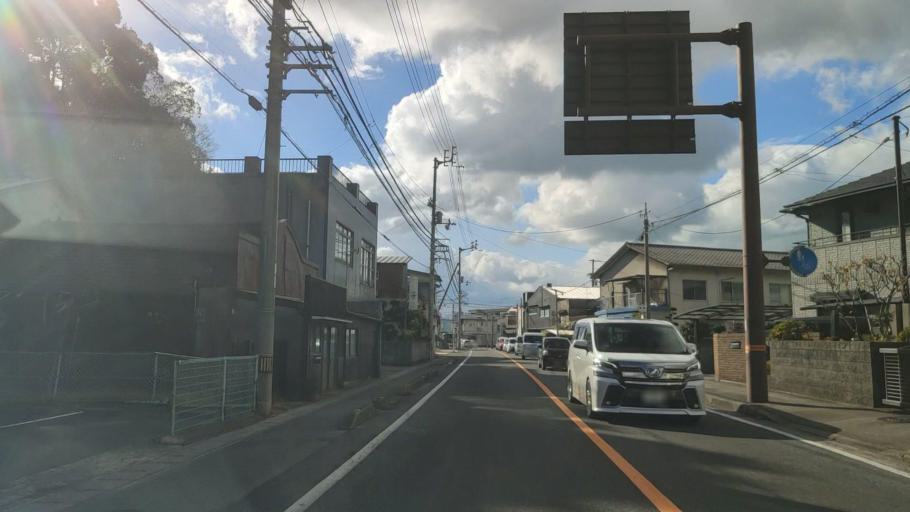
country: JP
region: Ehime
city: Masaki-cho
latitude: 33.8310
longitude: 132.7088
